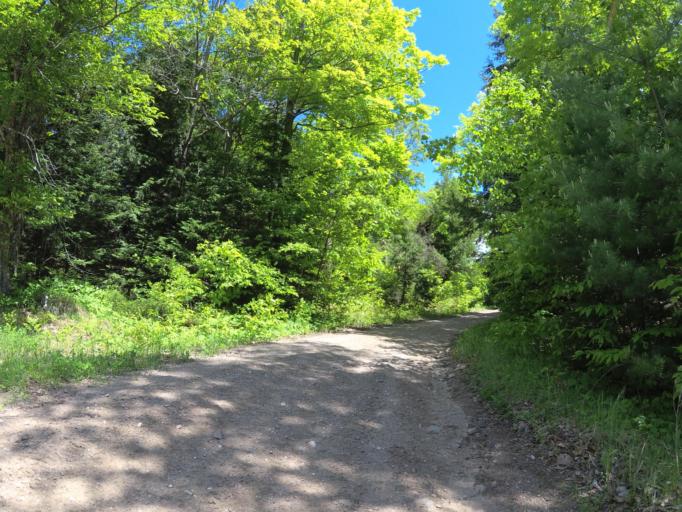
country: CA
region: Ontario
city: Renfrew
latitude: 45.0169
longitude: -76.8937
